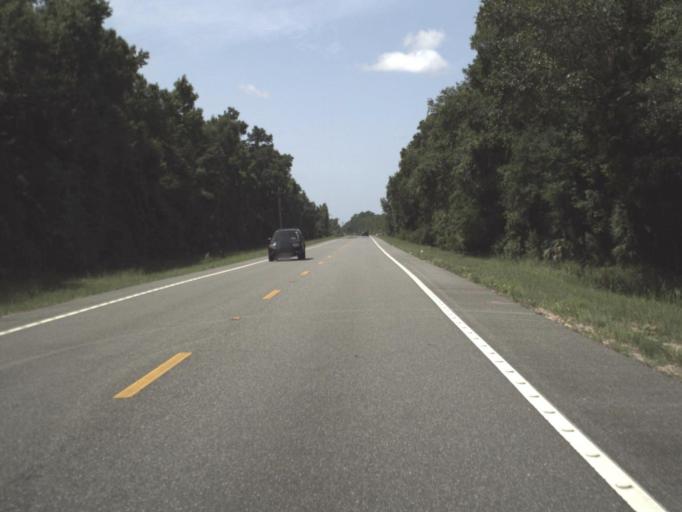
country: US
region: Florida
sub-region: Taylor County
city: Steinhatchee
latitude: 29.7488
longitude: -83.3533
